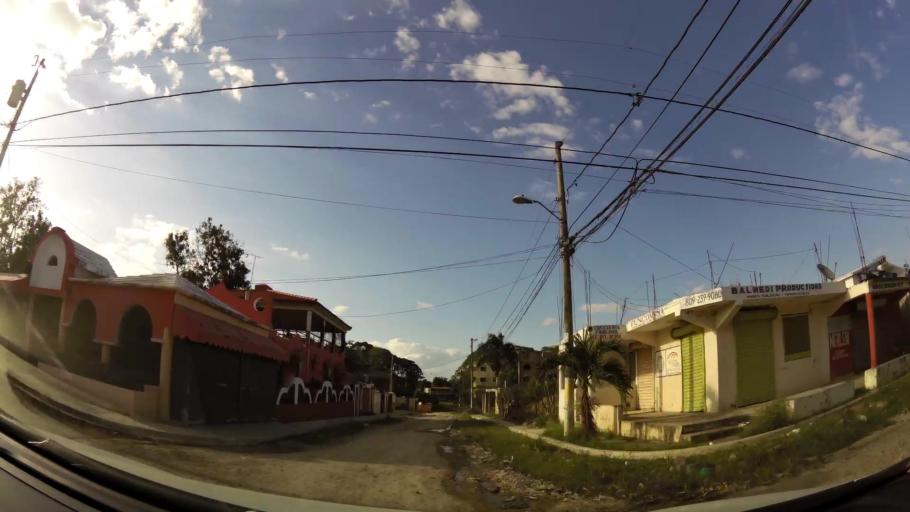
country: DO
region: Nacional
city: Ensanche Luperon
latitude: 18.5595
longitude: -69.8946
